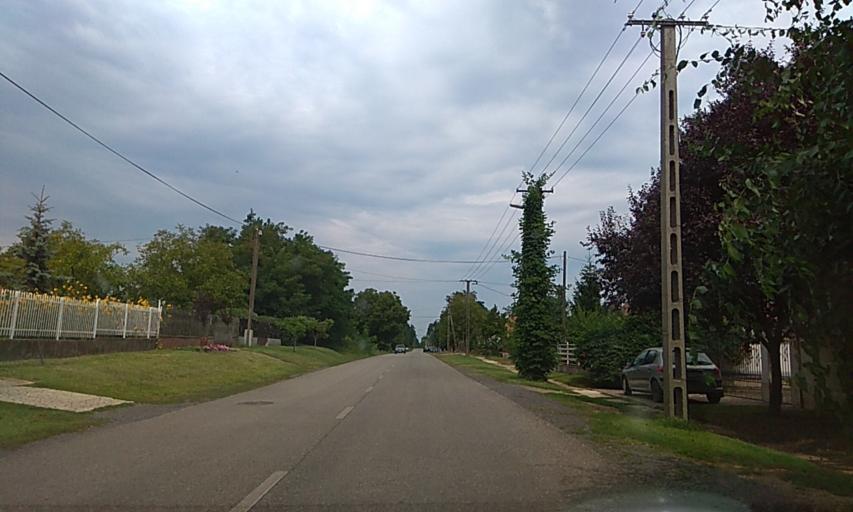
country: HU
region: Szabolcs-Szatmar-Bereg
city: Nyiregyhaza
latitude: 47.9946
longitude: 21.7053
